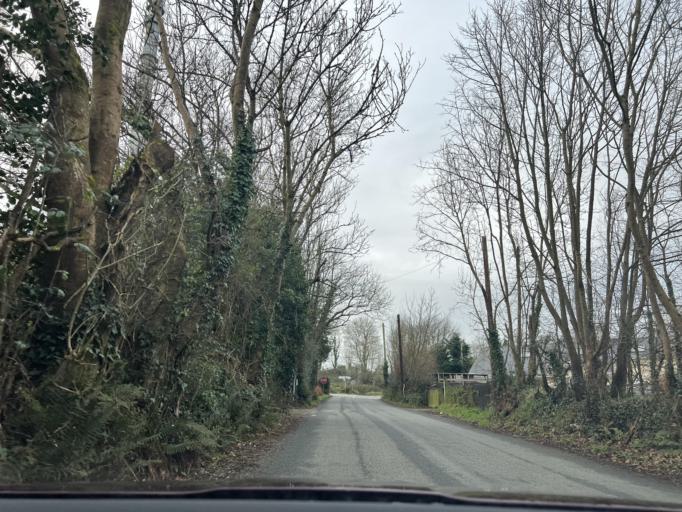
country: IE
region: Leinster
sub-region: Loch Garman
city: Enniscorthy
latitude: 52.3837
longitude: -6.5762
